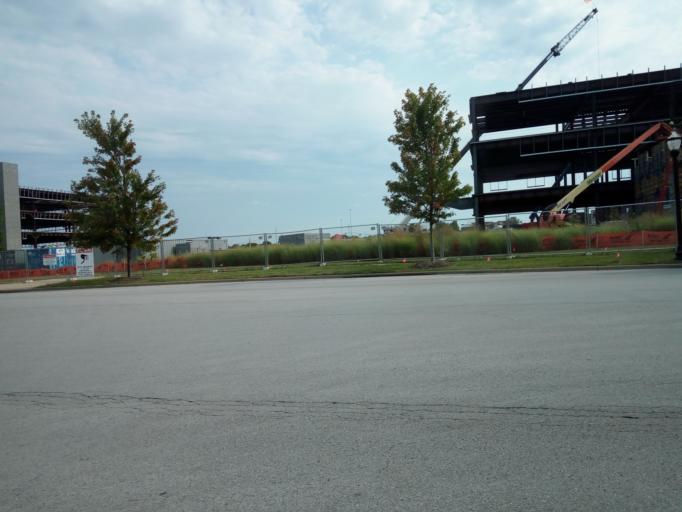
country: US
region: Kentucky
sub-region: Jefferson County
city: Worthington
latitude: 38.3150
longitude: -85.5746
